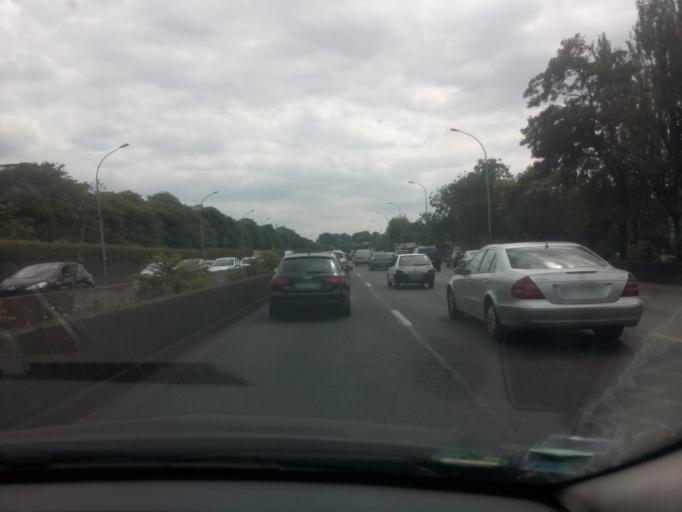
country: FR
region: Ile-de-France
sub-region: Departement du Val-de-Marne
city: Saint-Mande
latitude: 48.8394
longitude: 2.4133
